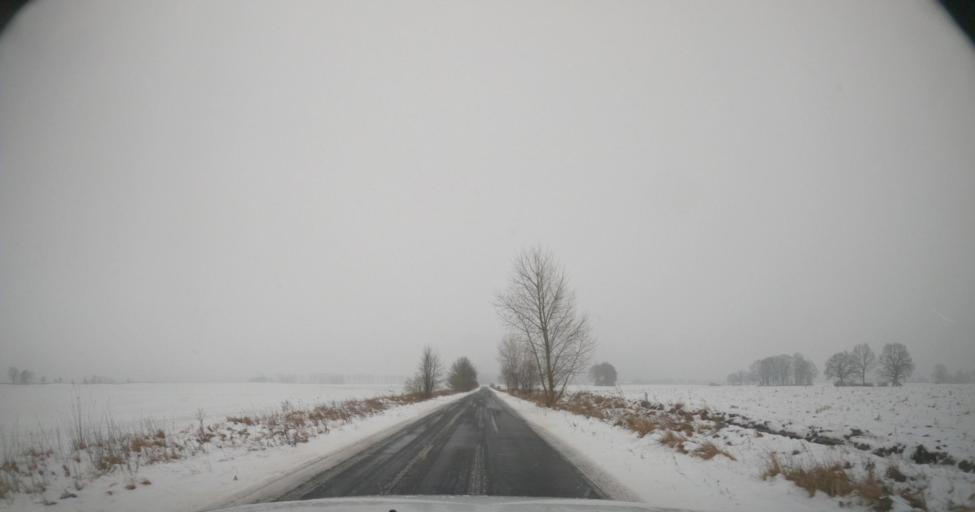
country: PL
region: West Pomeranian Voivodeship
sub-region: Powiat gryficki
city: Brojce
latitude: 53.8888
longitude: 15.3877
